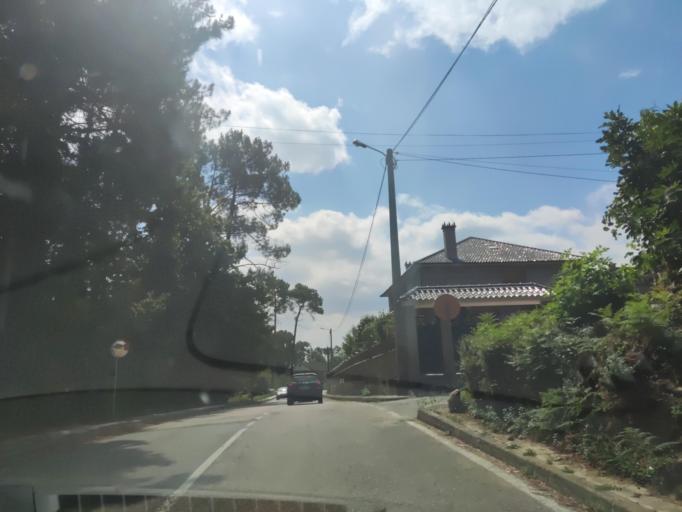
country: ES
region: Galicia
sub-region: Provincia de Pontevedra
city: Porrino
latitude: 42.1486
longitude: -8.6490
